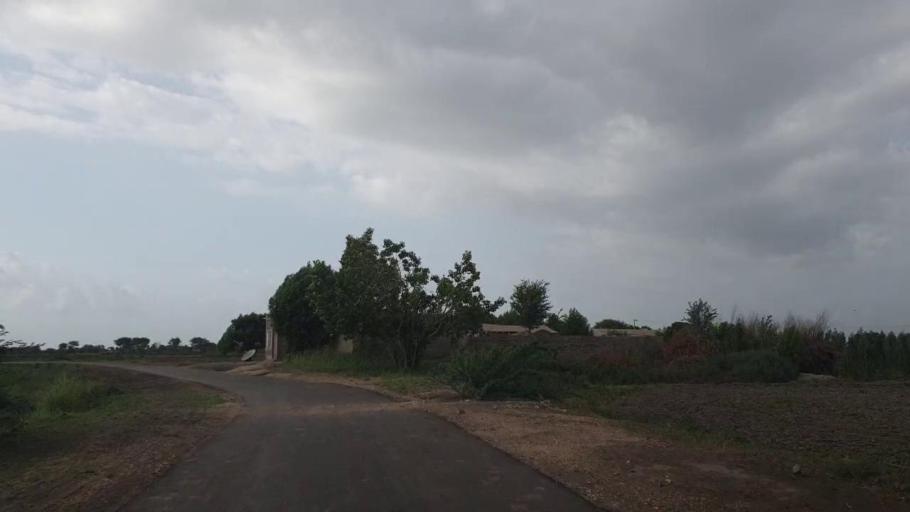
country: PK
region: Sindh
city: Kadhan
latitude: 24.6006
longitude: 69.0565
